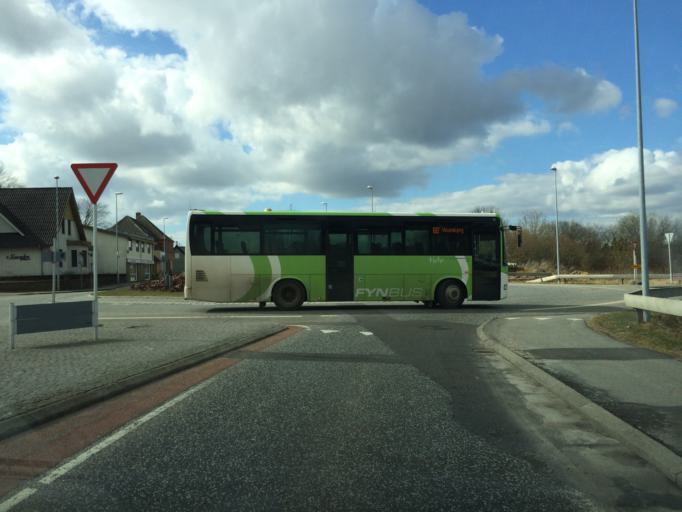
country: DK
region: South Denmark
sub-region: Assens Kommune
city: Tommerup Stationsby
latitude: 55.3875
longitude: 10.1964
